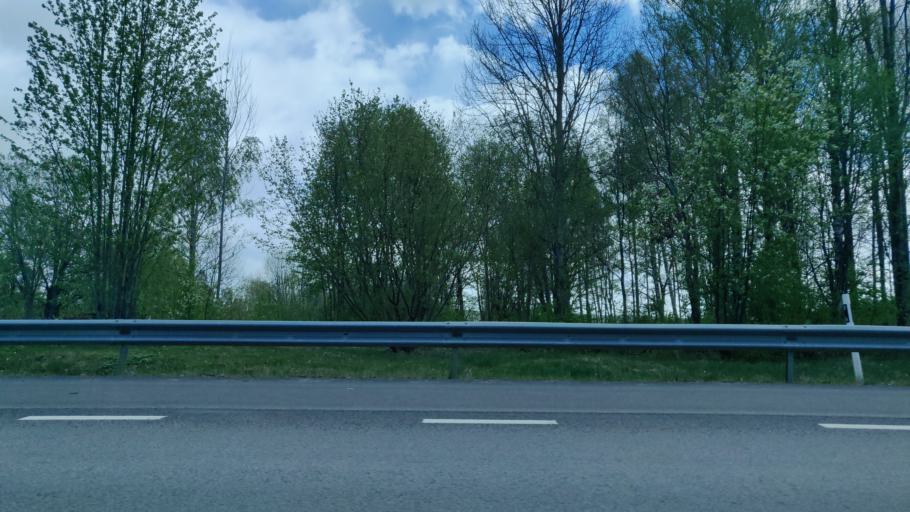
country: SE
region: Vaermland
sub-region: Karlstads Kommun
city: Molkom
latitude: 59.5996
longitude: 13.7366
